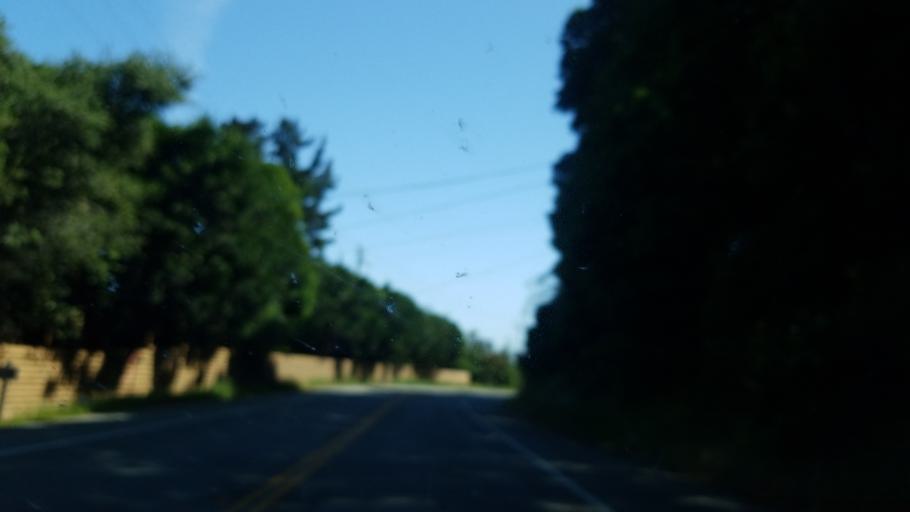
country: US
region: California
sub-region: Santa Cruz County
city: Soquel
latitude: 37.0203
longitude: -121.9517
